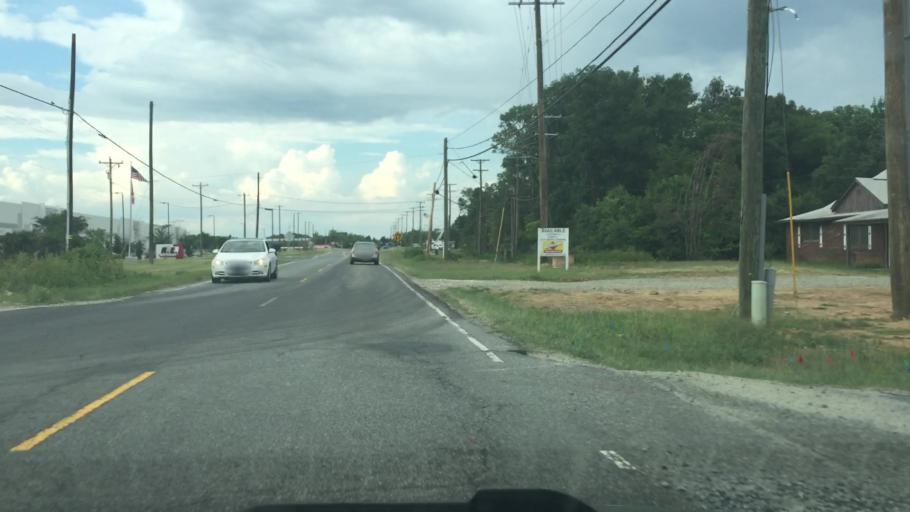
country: US
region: North Carolina
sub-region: Cabarrus County
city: Harrisburg
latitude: 35.4016
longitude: -80.7154
